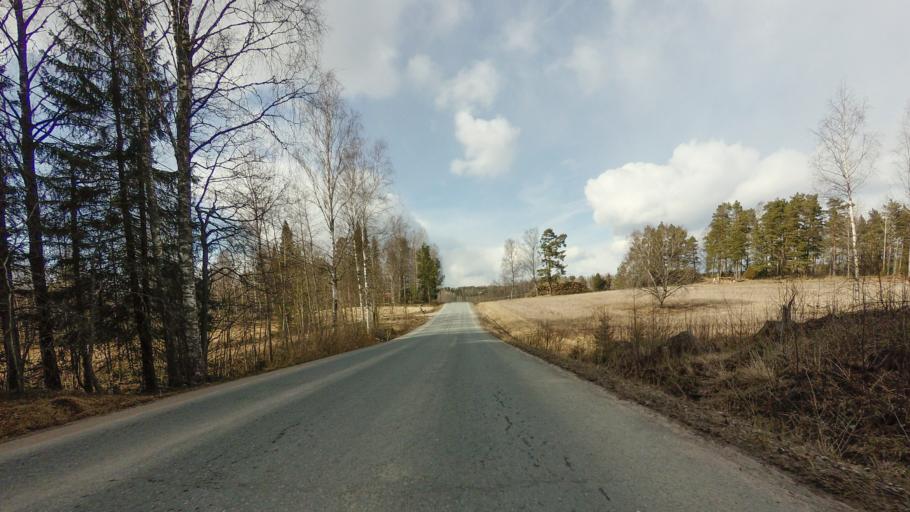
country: FI
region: Varsinais-Suomi
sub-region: Salo
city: Suomusjaervi
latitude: 60.3344
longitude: 23.7037
